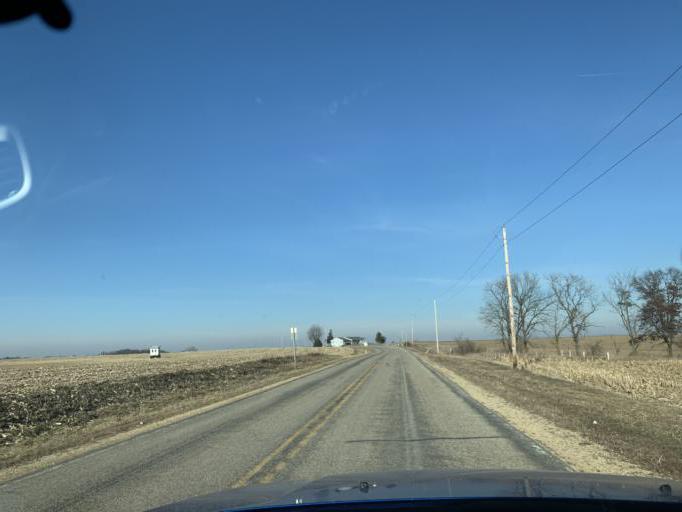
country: US
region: Wisconsin
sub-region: Iowa County
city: Barneveld
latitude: 42.8163
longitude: -89.9167
